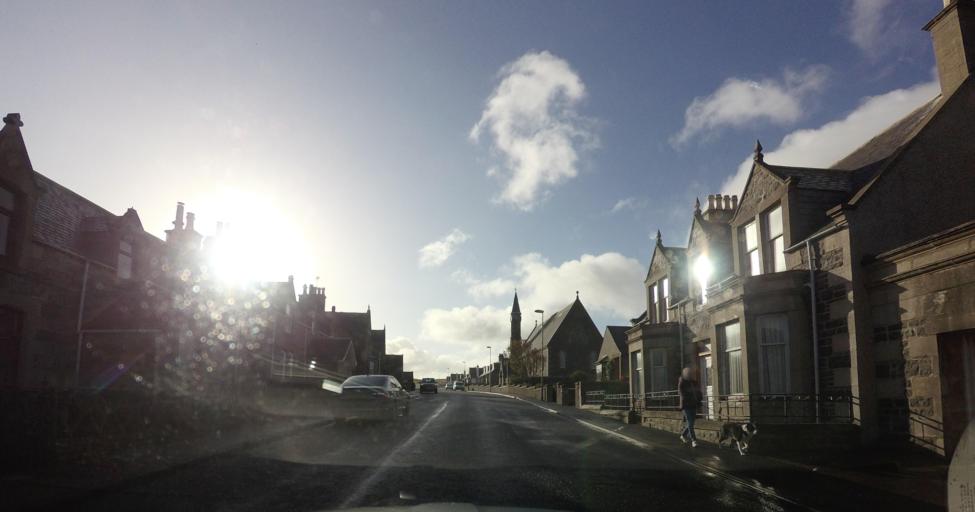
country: GB
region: Scotland
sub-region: Aberdeenshire
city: Whitehills
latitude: 57.6763
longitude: -2.5797
